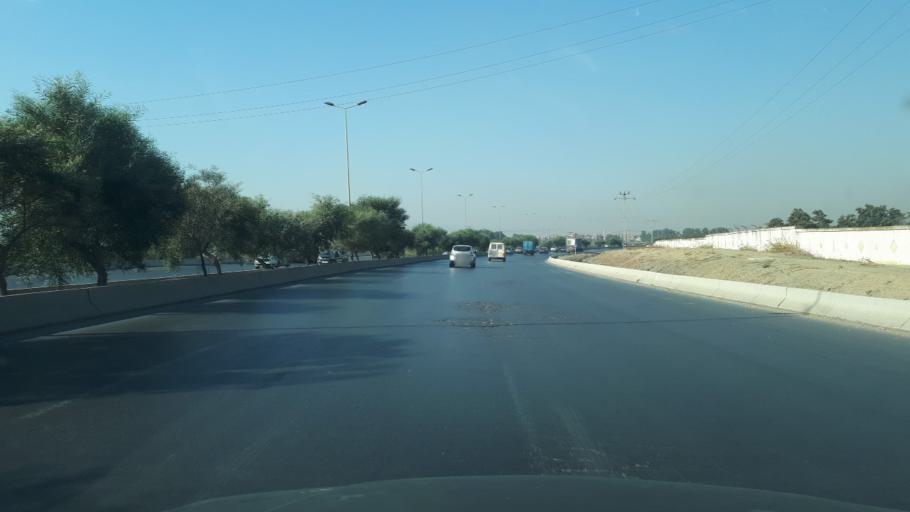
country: DZ
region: Tipaza
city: Baraki
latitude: 36.6839
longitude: 3.1108
